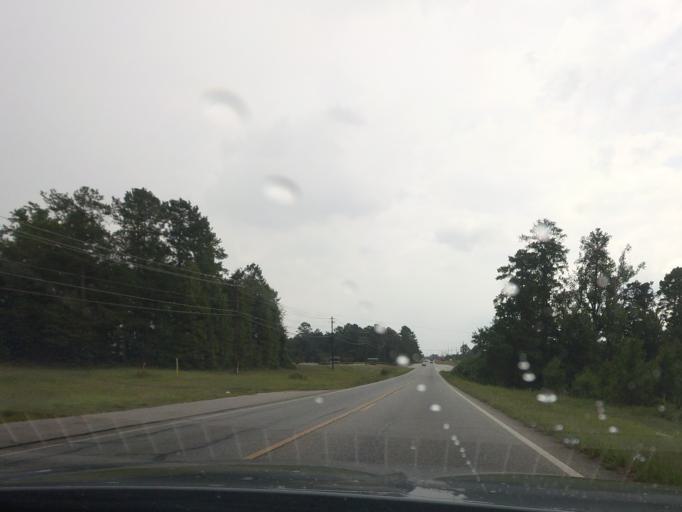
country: US
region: Georgia
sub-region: Bibb County
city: West Point
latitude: 32.8412
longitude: -83.7518
